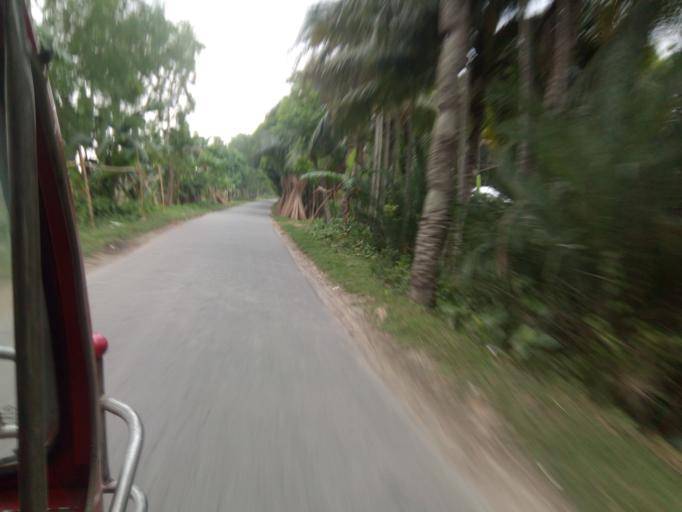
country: BD
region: Khulna
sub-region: Magura
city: Magura
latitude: 23.5237
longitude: 89.6142
